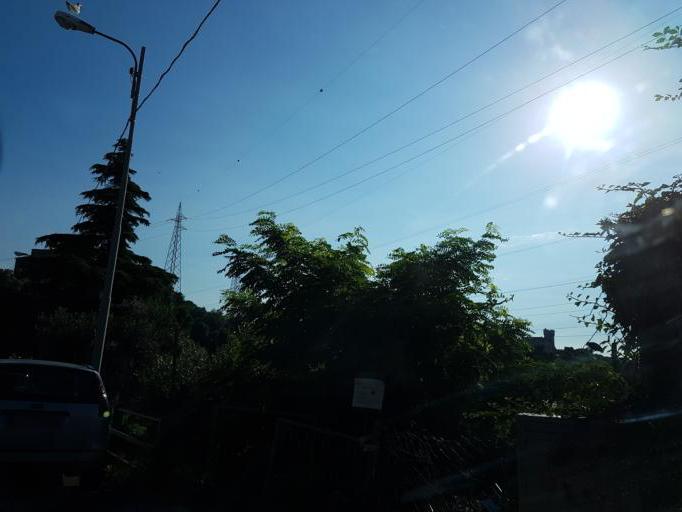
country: IT
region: Liguria
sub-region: Provincia di Genova
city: San Teodoro
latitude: 44.4272
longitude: 8.8676
